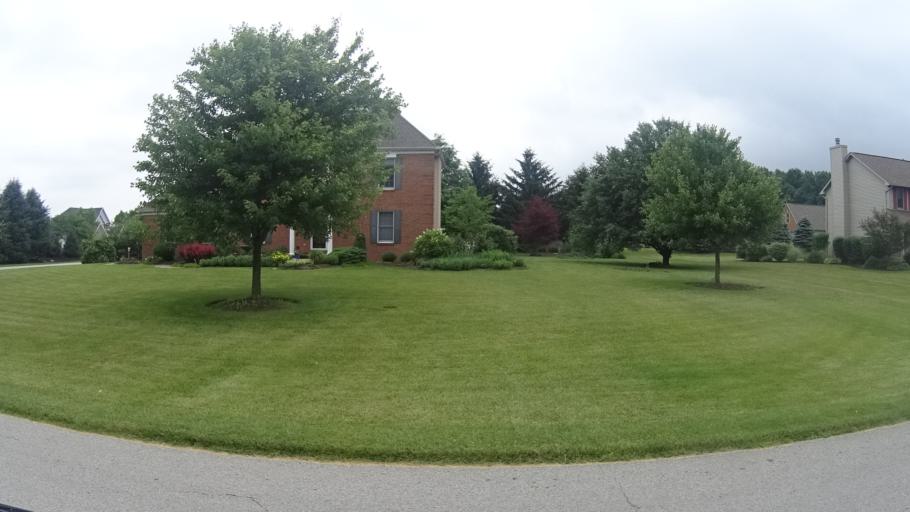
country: US
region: Ohio
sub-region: Erie County
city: Milan
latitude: 41.2953
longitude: -82.5820
